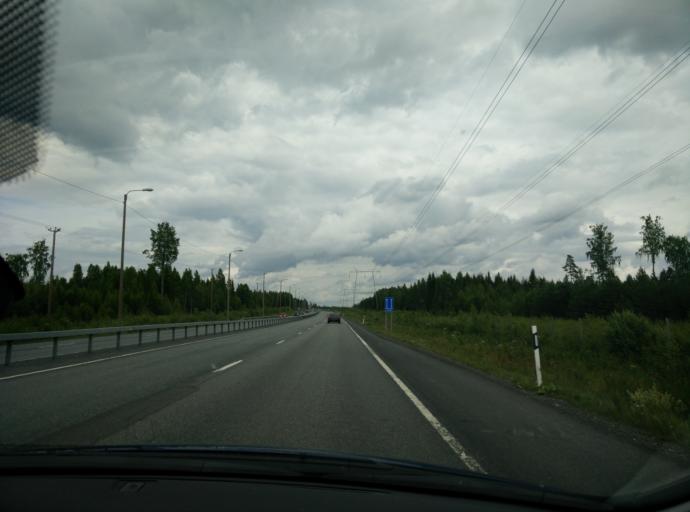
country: FI
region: Pirkanmaa
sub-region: Tampere
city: Kangasala
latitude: 61.6079
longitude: 24.1425
